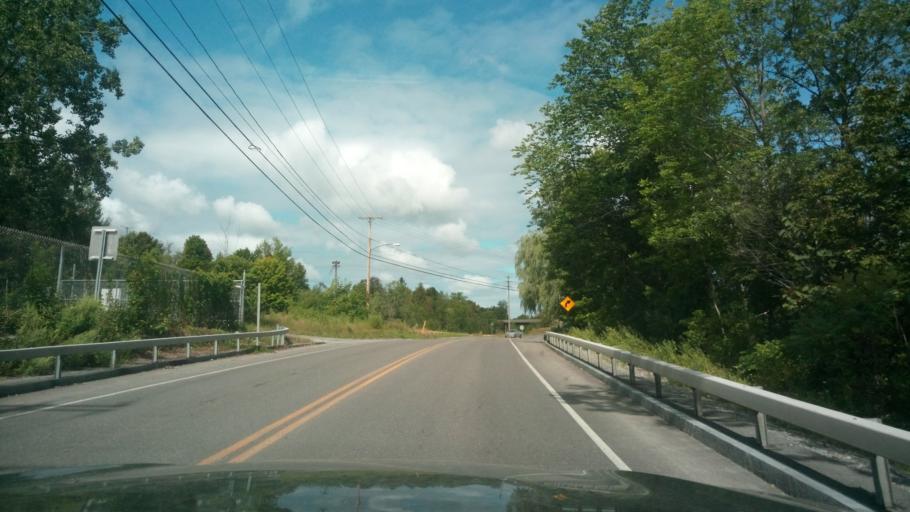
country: US
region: New York
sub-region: Onondaga County
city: East Syracuse
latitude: 43.0018
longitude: -76.0755
